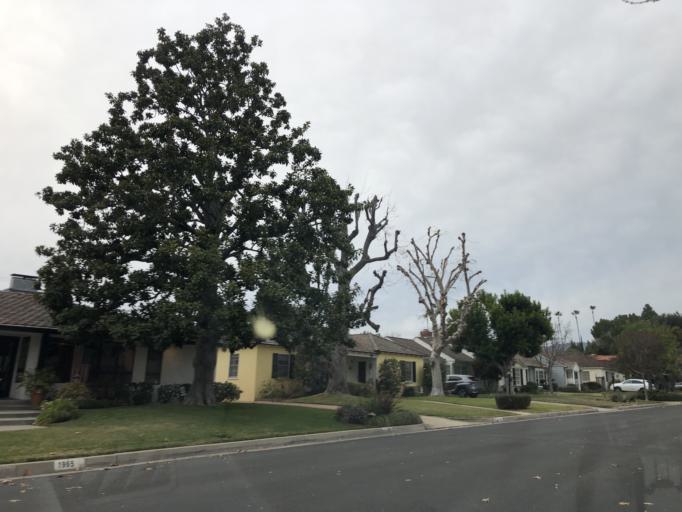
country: US
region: California
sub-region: Los Angeles County
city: San Marino
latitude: 34.1158
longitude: -118.0949
